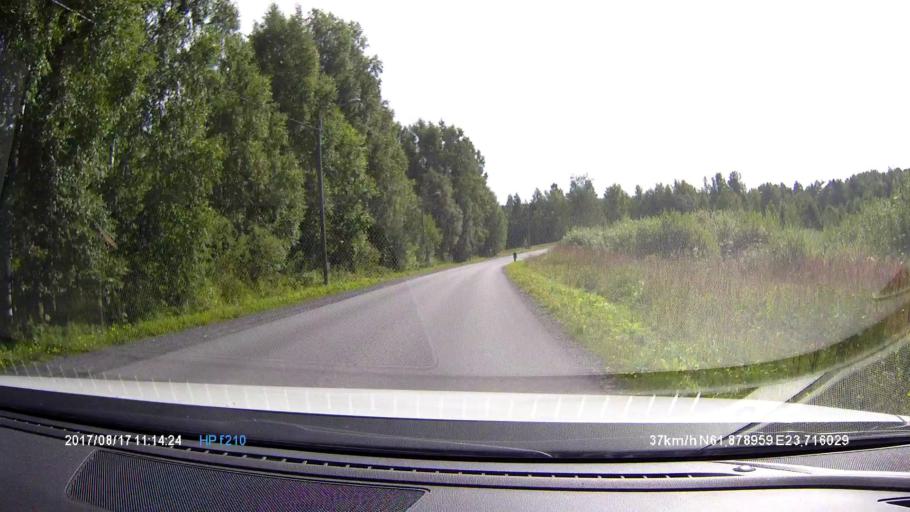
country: FI
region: Pirkanmaa
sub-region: Tampere
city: Kuru
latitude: 61.8789
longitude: 23.7162
